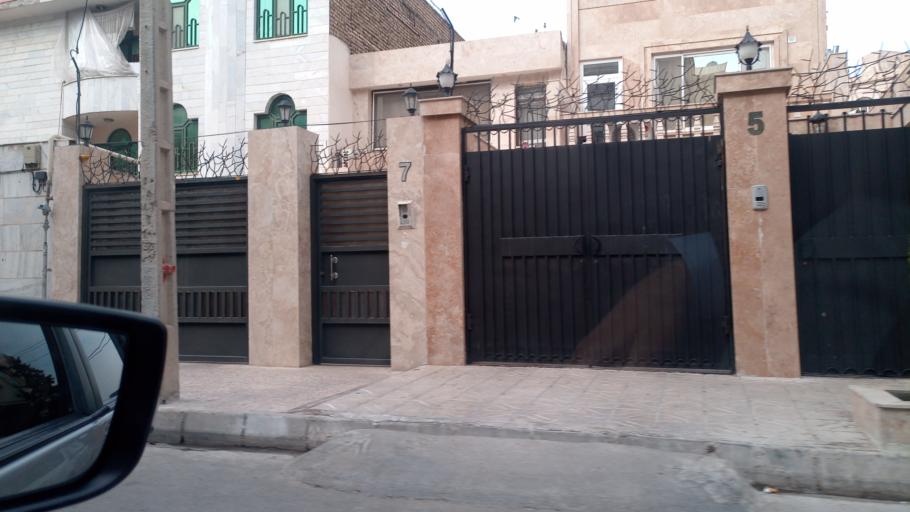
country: IR
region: Razavi Khorasan
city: Mashhad
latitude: 36.3112
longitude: 59.5107
